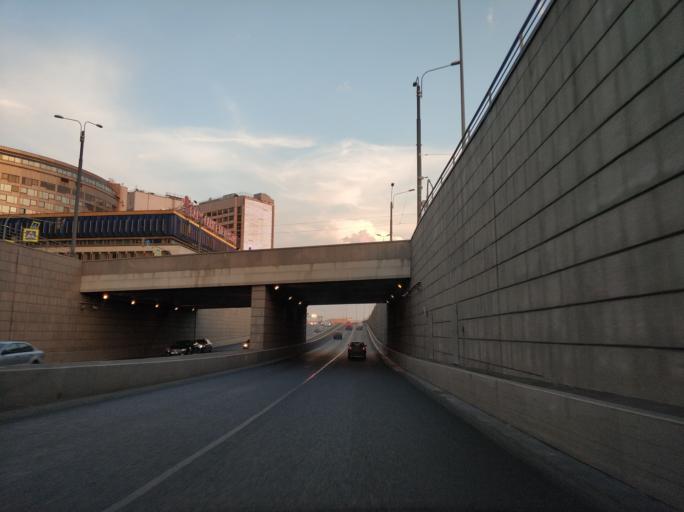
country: RU
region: Leningrad
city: Sampsonievskiy
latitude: 59.9585
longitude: 30.3392
